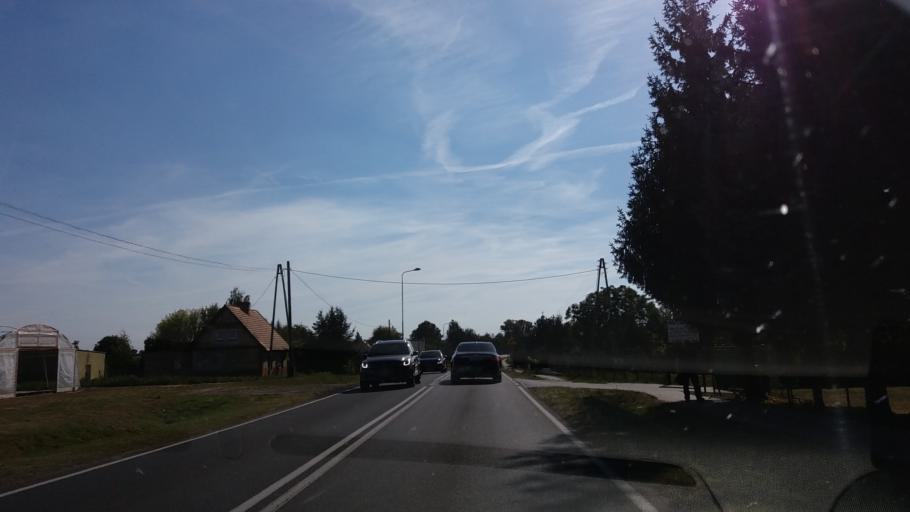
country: PL
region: Greater Poland Voivodeship
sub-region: Powiat miedzychodzki
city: Miedzychod
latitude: 52.5802
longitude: 15.8983
